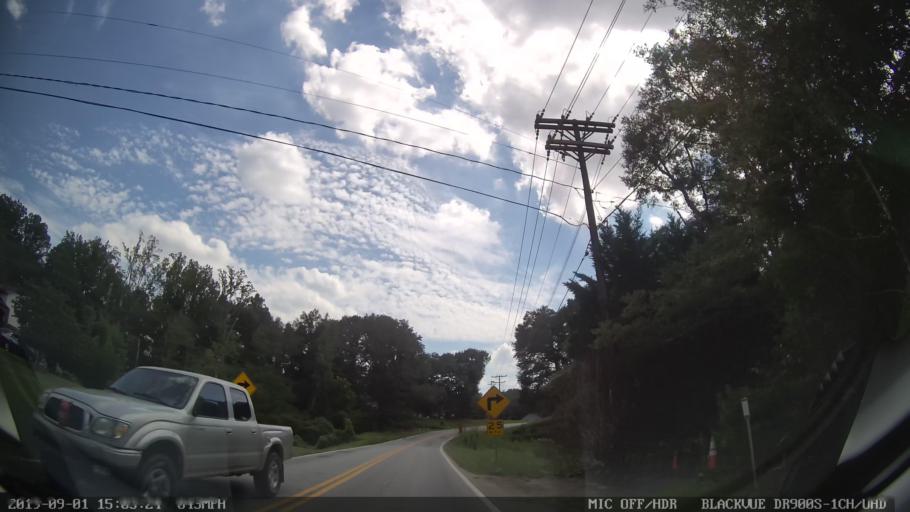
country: US
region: South Carolina
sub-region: Greenville County
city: Greer
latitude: 34.9638
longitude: -82.2013
